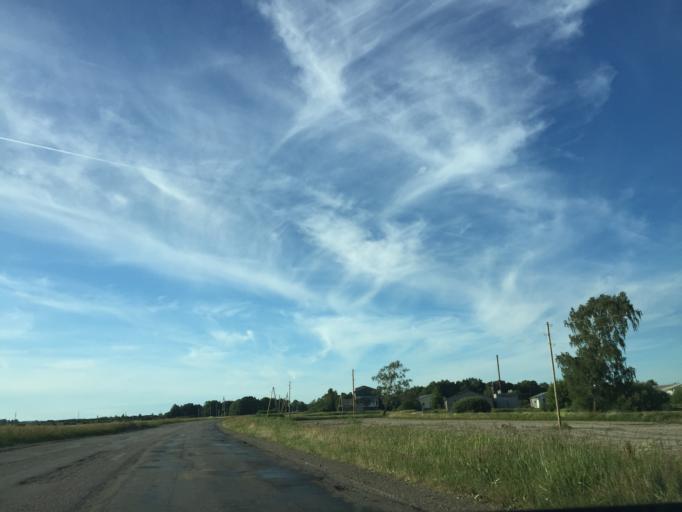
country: LV
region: Ventspils
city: Ventspils
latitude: 57.3102
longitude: 21.5563
